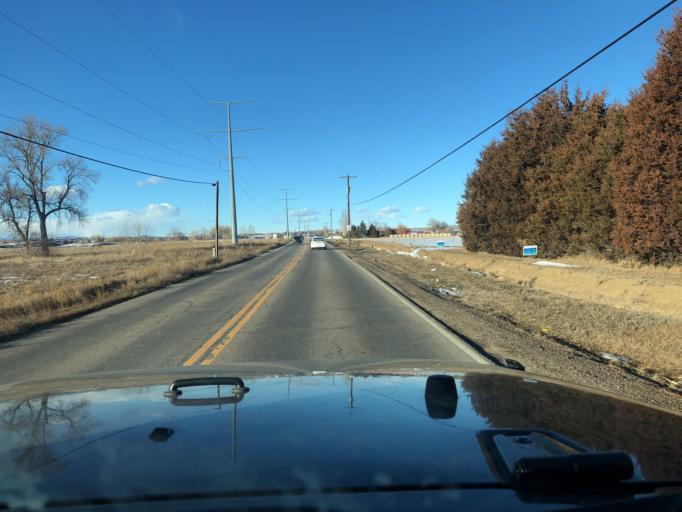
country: US
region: Colorado
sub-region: Boulder County
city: Longmont
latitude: 40.1837
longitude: -105.0552
